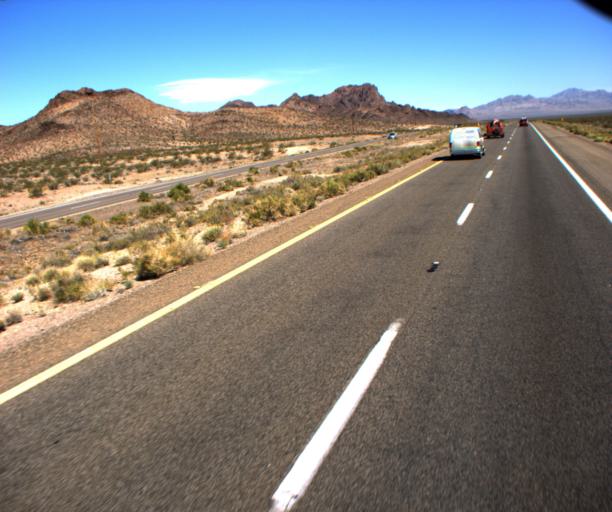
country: US
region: Arizona
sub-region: Mohave County
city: Dolan Springs
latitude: 35.7608
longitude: -114.5072
